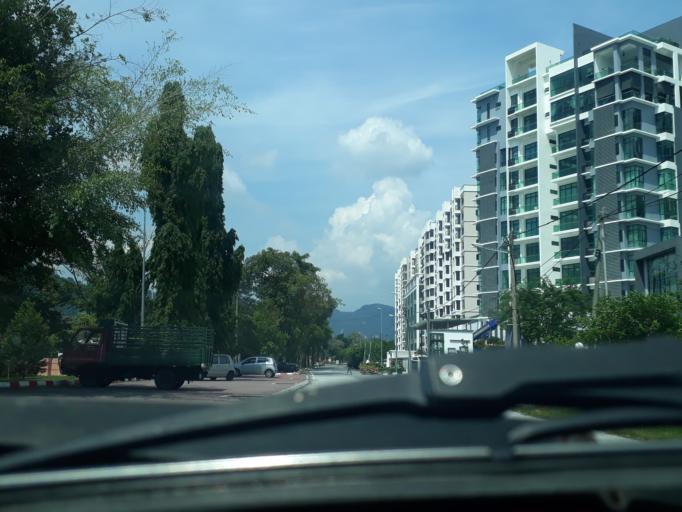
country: MY
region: Perak
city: Ipoh
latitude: 4.5949
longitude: 101.1131
